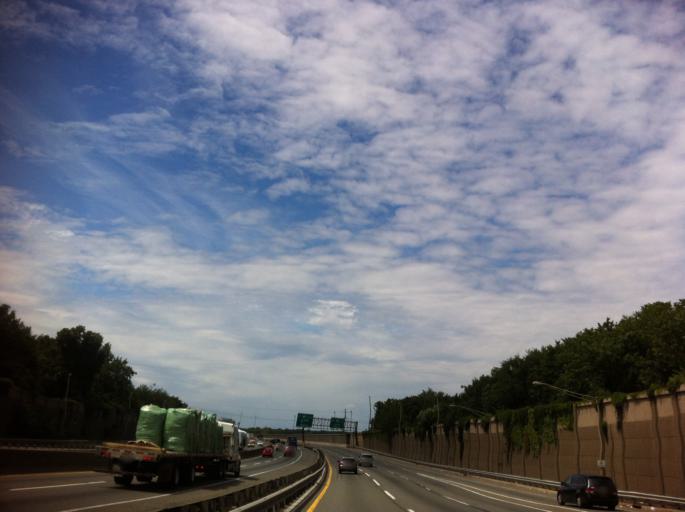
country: US
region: New Jersey
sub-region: Bergen County
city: Leonia
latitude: 40.8720
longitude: -73.9798
